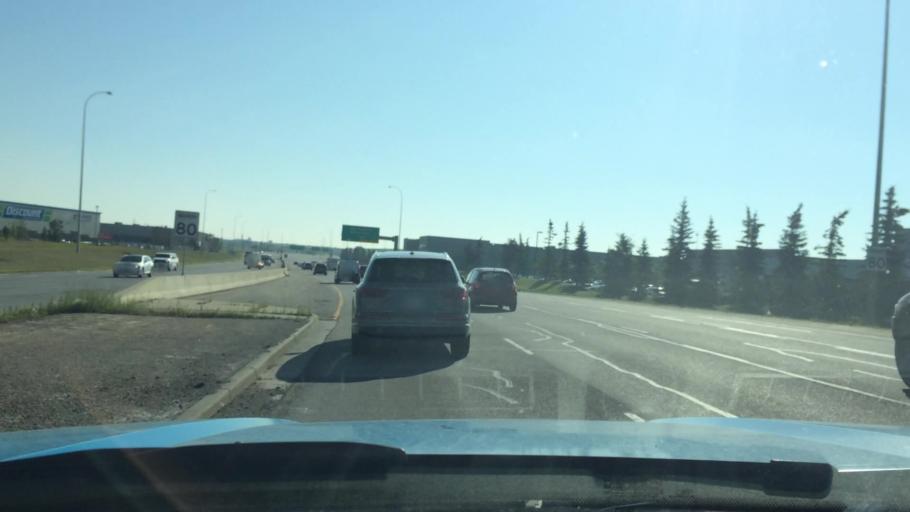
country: CA
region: Alberta
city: Calgary
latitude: 51.0929
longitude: -113.9986
